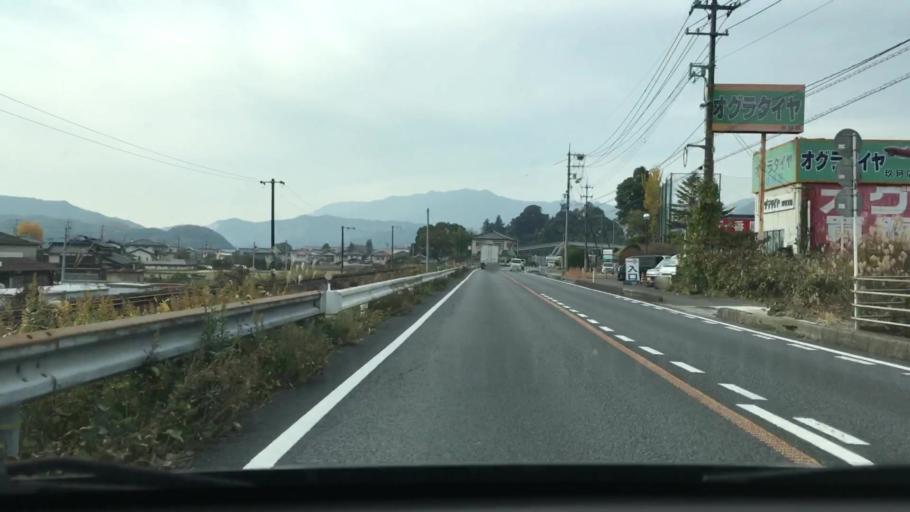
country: JP
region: Yamaguchi
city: Yanai
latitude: 34.0919
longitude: 132.0595
